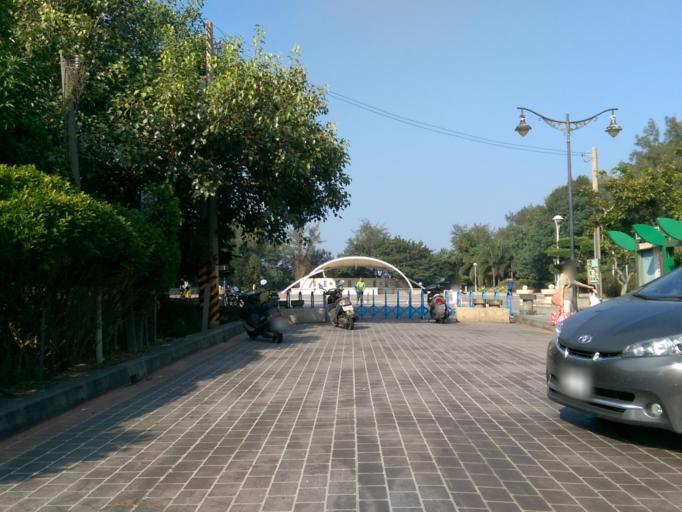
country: TW
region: Taiwan
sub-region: Yunlin
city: Douliu
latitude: 23.7530
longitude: 120.2541
